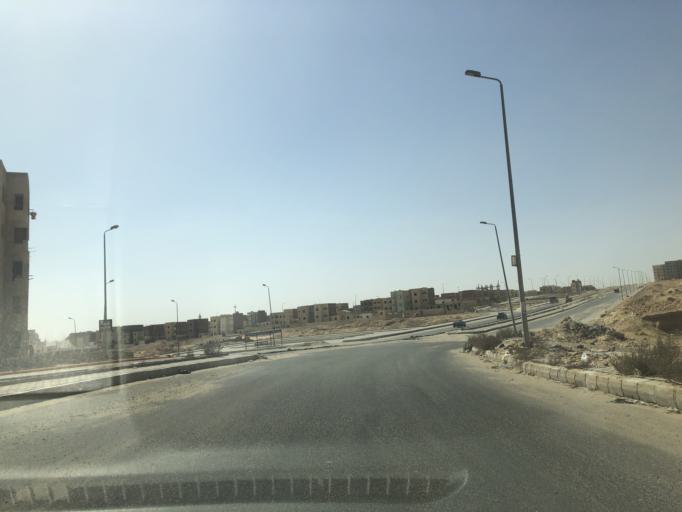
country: EG
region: Al Jizah
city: Madinat Sittah Uktubar
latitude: 29.9302
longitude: 31.0133
